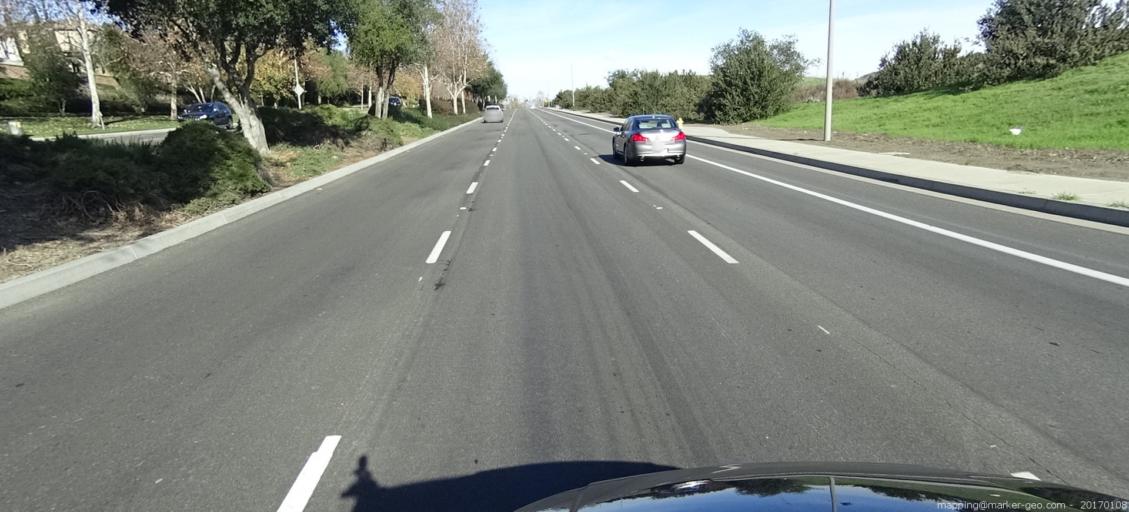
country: US
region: California
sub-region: Orange County
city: Ladera Ranch
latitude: 33.5413
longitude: -117.6271
